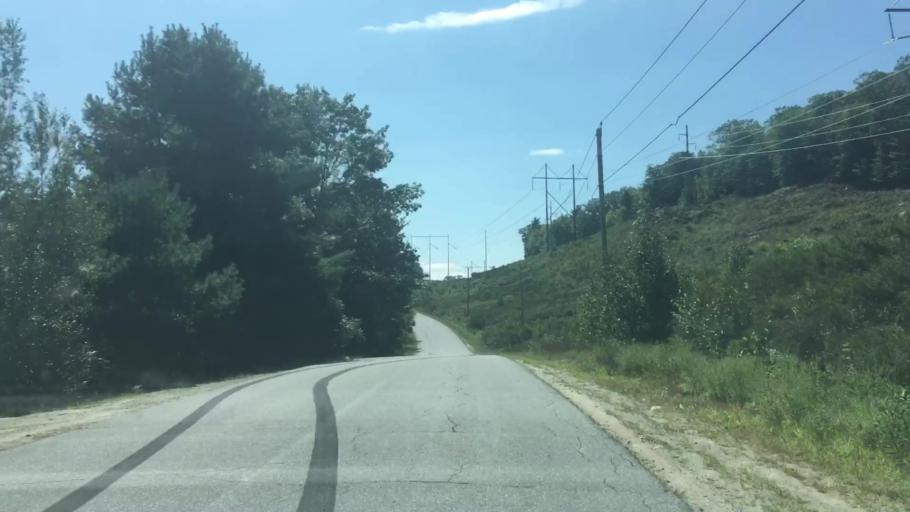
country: US
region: Maine
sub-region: Kennebec County
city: Monmouth
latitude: 44.2002
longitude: -69.9612
